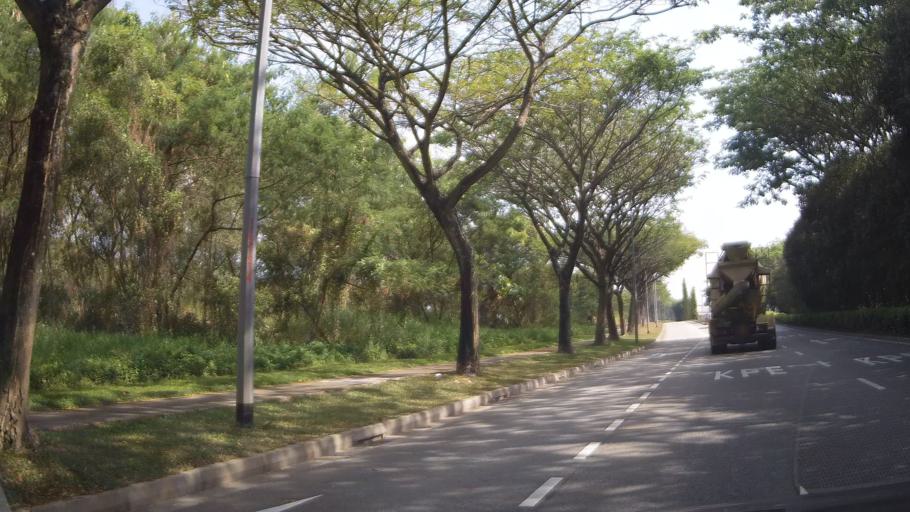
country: SG
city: Singapore
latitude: 1.3666
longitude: 103.9065
